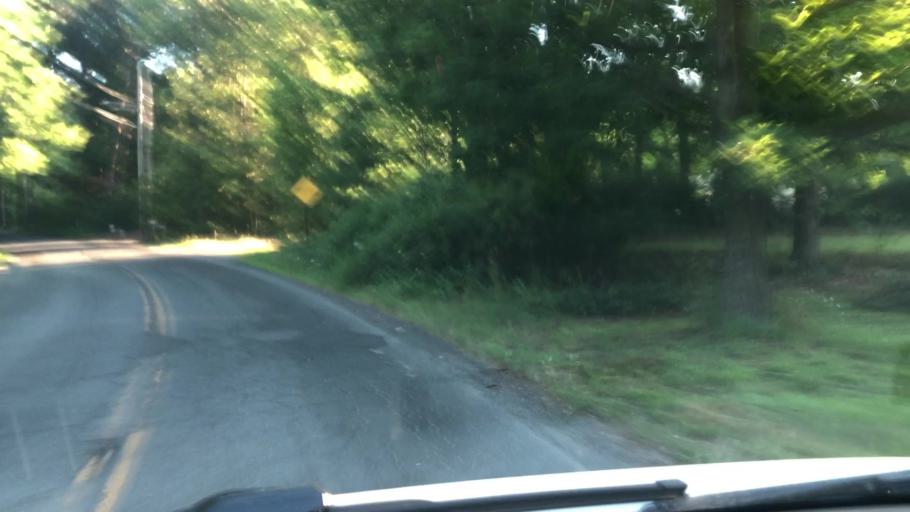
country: US
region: Massachusetts
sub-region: Hampshire County
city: Easthampton
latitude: 42.2871
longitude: -72.7142
